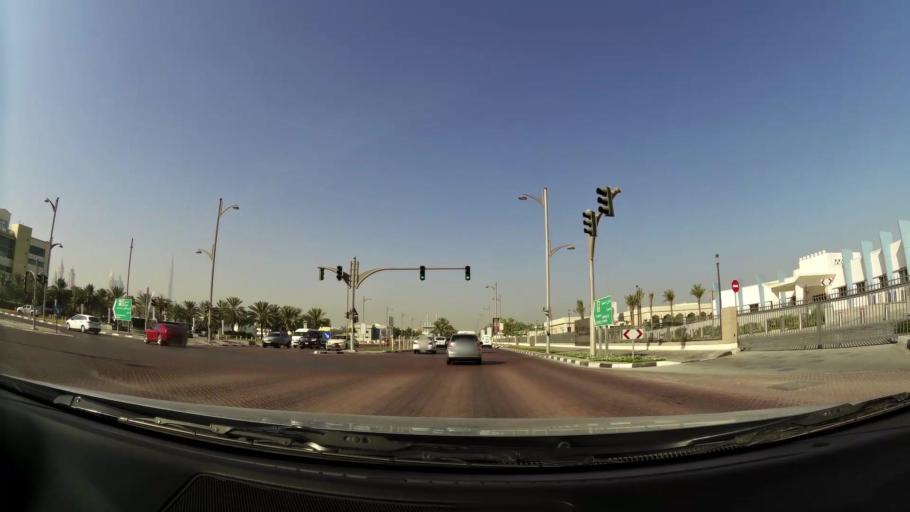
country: AE
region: Ash Shariqah
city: Sharjah
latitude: 25.2406
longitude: 55.2696
